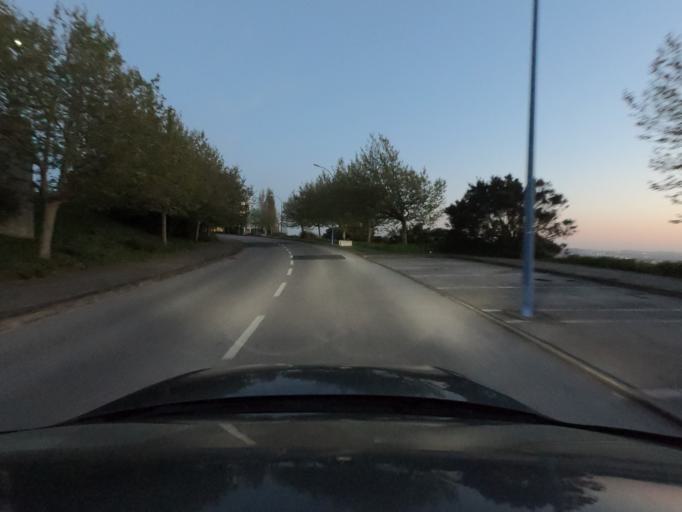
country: PT
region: Lisbon
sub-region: Oeiras
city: Porto Salvo
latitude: 38.7405
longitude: -9.3060
